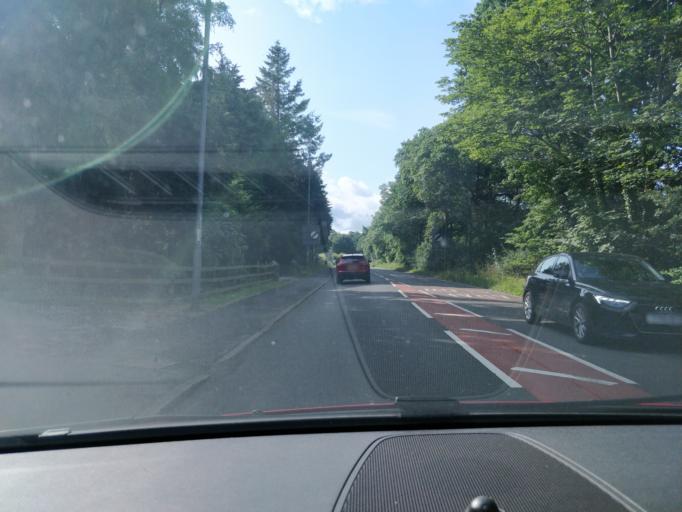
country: GB
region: Wales
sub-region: Conwy
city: Llansantffraid Glan Conwy
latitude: 53.2625
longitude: -3.7991
